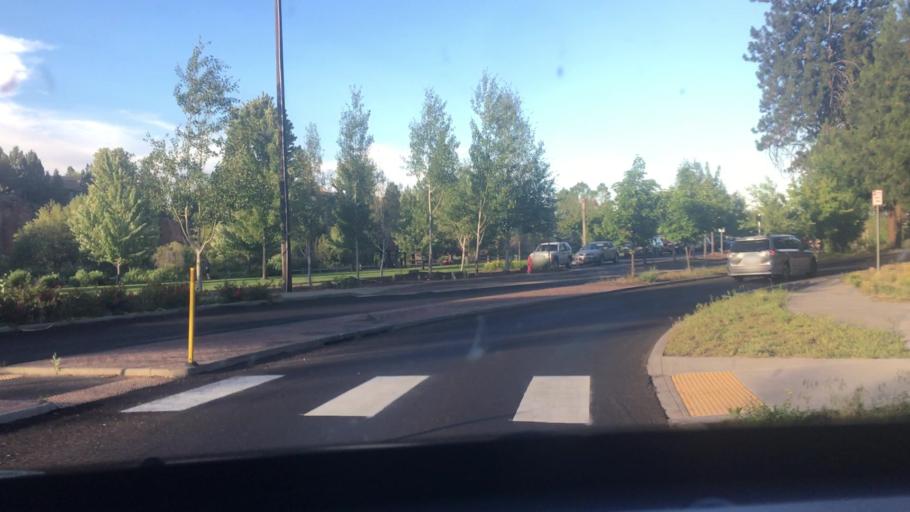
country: US
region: Oregon
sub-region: Deschutes County
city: Bend
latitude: 44.0408
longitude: -121.3278
